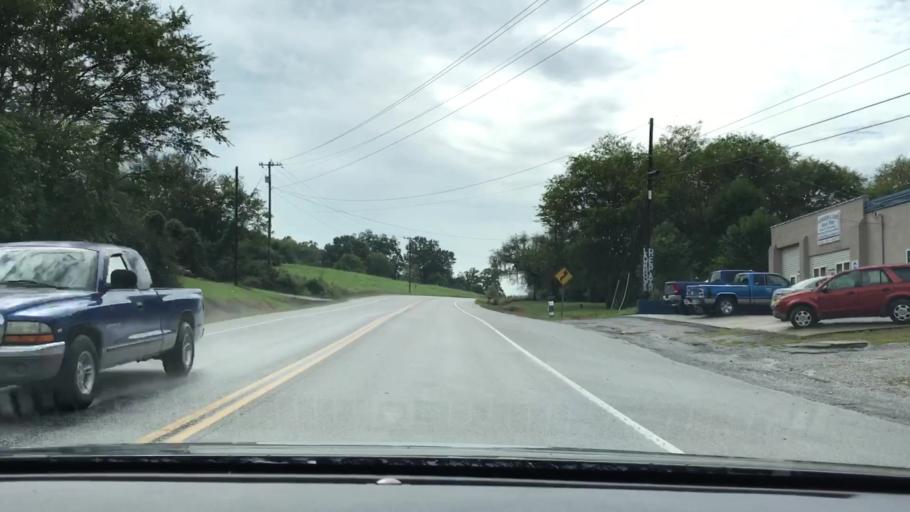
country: US
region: Tennessee
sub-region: Smith County
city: Carthage
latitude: 36.3033
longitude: -85.9759
